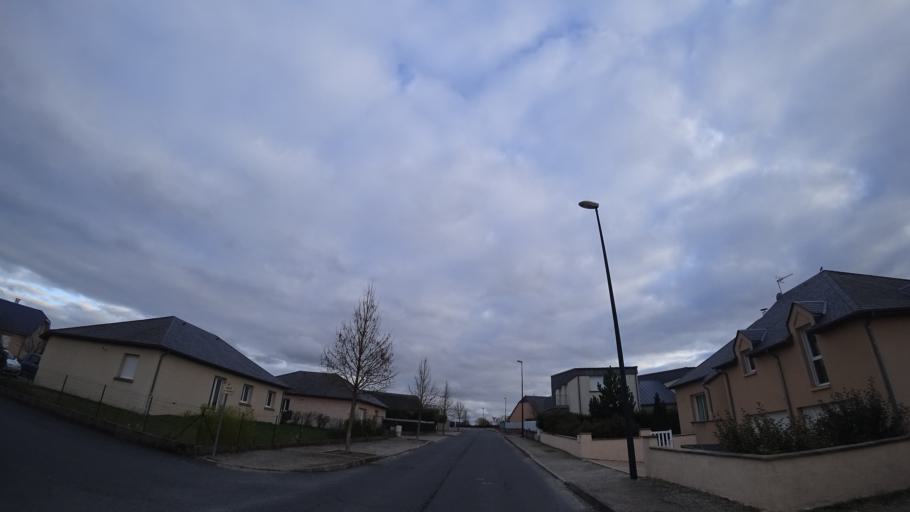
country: FR
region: Midi-Pyrenees
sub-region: Departement de l'Aveyron
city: Le Monastere
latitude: 44.3355
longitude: 2.5747
